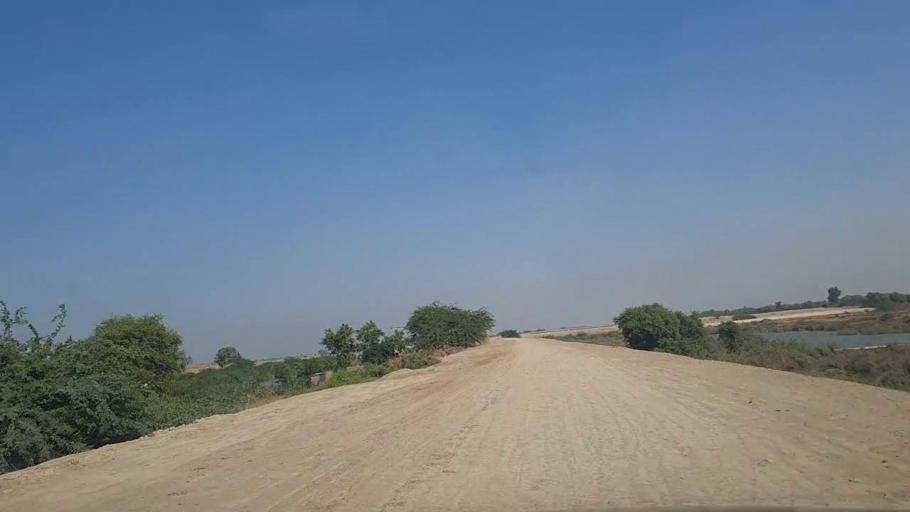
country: PK
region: Sindh
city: Daro Mehar
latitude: 24.8965
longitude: 68.0704
